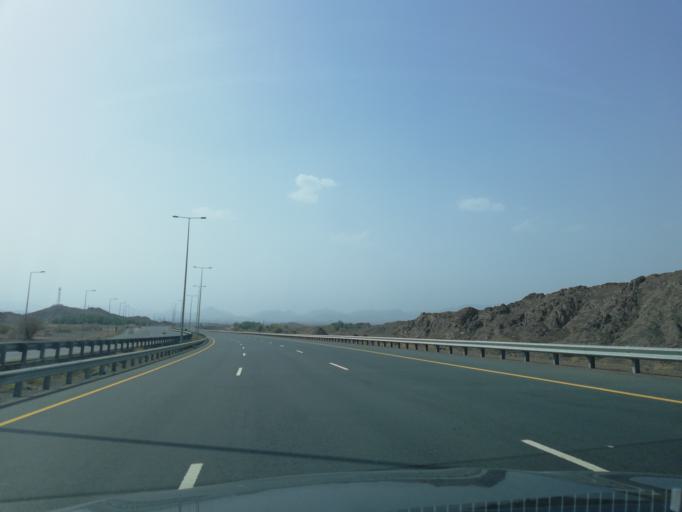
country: OM
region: Muhafazat ad Dakhiliyah
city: Sufalat Sama'il
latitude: 23.0047
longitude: 58.2294
